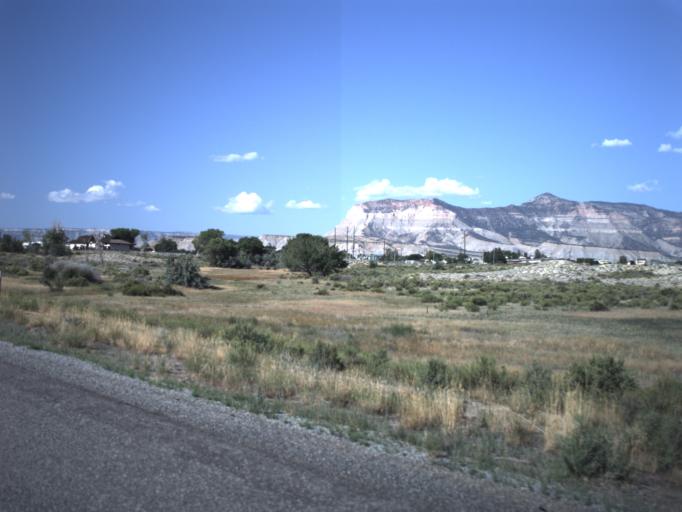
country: US
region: Utah
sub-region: Emery County
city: Huntington
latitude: 39.3373
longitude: -110.9639
